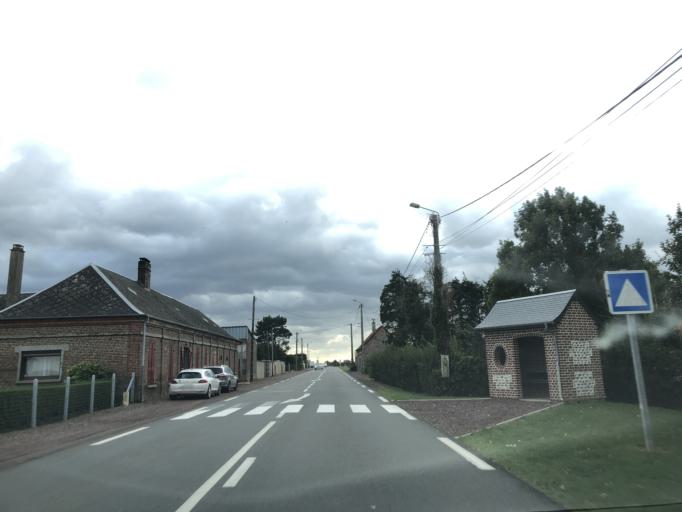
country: FR
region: Picardie
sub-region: Departement de la Somme
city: Pende
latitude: 50.1522
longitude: 1.5488
